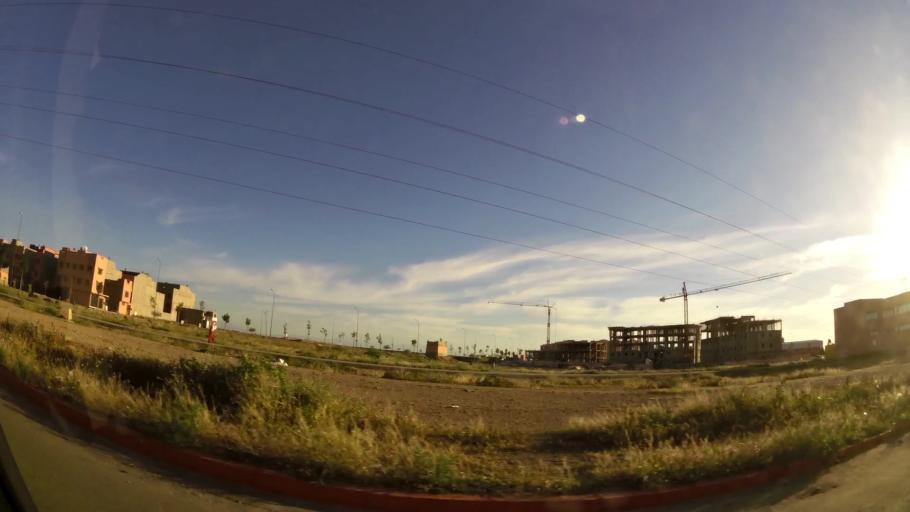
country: MA
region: Marrakech-Tensift-Al Haouz
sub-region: Marrakech
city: Marrakesh
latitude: 31.7434
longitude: -8.1237
